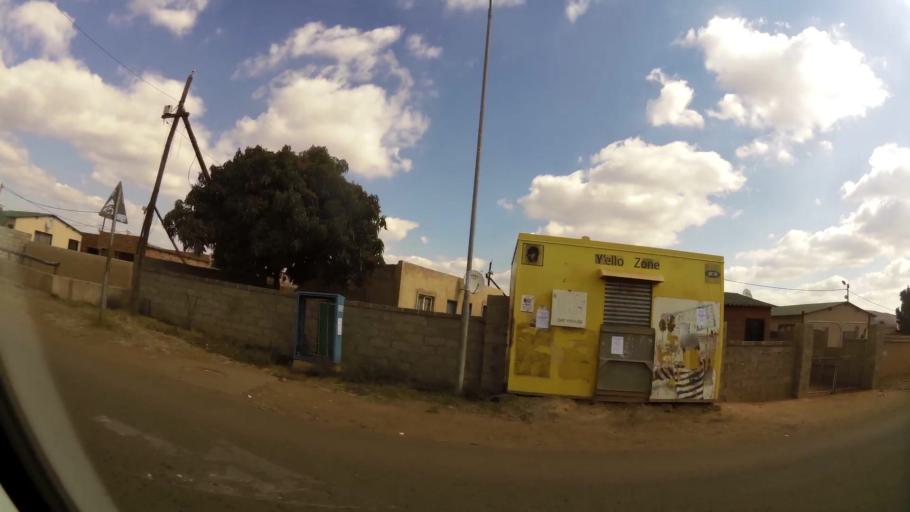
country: ZA
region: Gauteng
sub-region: City of Tshwane Metropolitan Municipality
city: Cullinan
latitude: -25.7089
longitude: 28.4022
